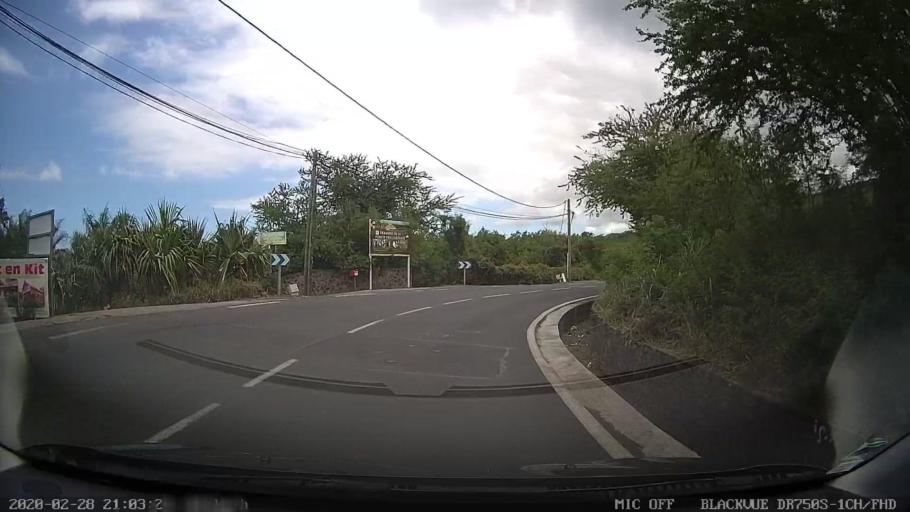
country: RE
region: Reunion
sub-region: Reunion
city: Saint-Leu
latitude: -21.1409
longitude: 55.2832
